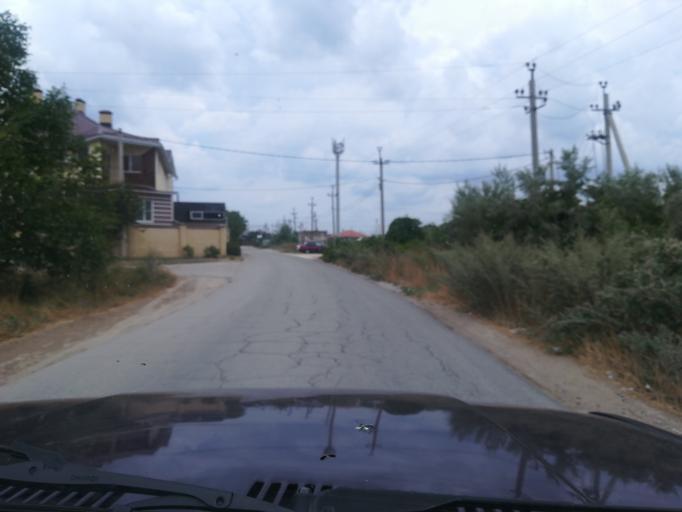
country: RU
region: Krasnodarskiy
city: Vityazevo
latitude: 45.0154
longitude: 37.2963
